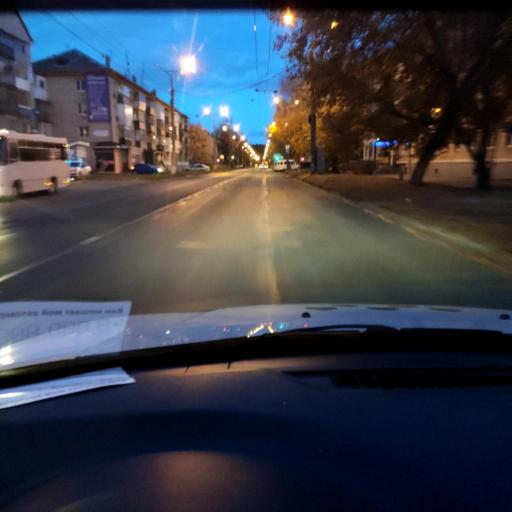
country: RU
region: Samara
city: Tol'yatti
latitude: 53.5067
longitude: 49.4021
